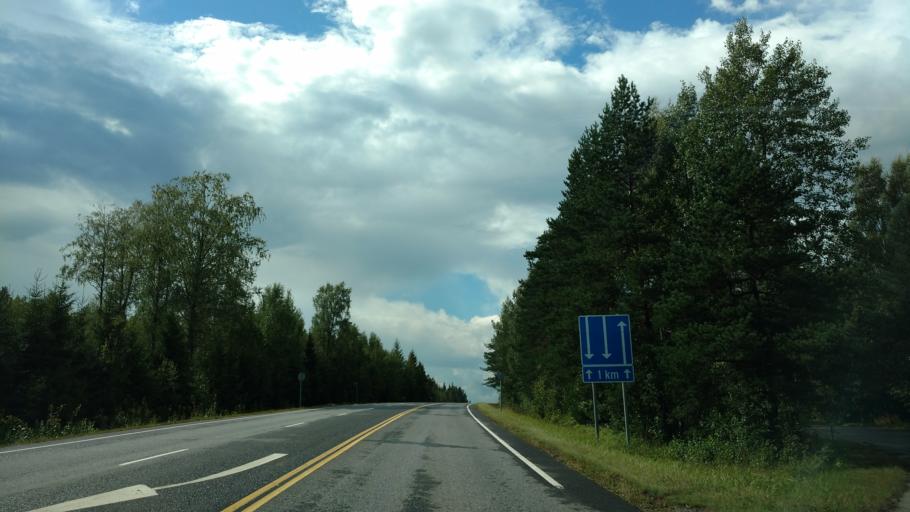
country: FI
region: Varsinais-Suomi
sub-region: Salo
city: Halikko
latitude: 60.3781
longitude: 22.9204
